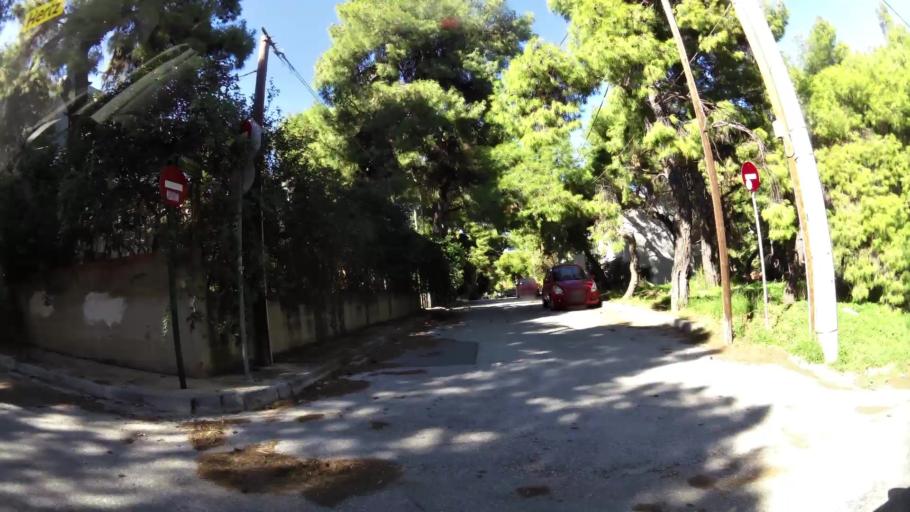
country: GR
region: Attica
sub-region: Nomarchia Anatolikis Attikis
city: Leondarion
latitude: 37.9853
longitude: 23.8597
